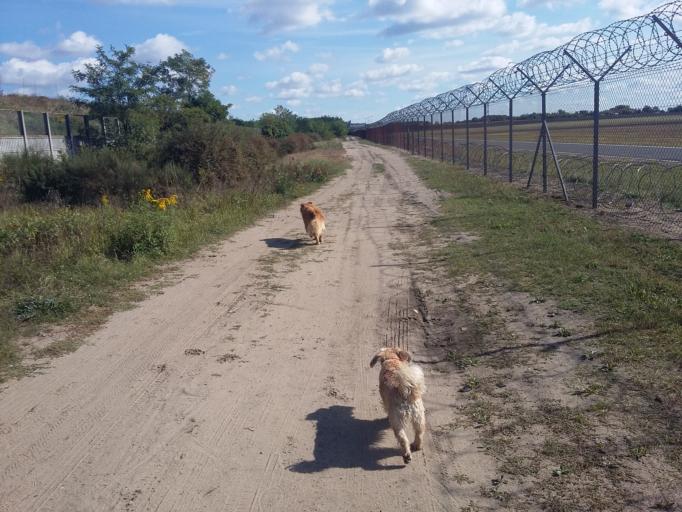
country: PL
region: Lodz Voivodeship
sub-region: Powiat pabianicki
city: Ksawerow
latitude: 51.7228
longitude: 19.3913
